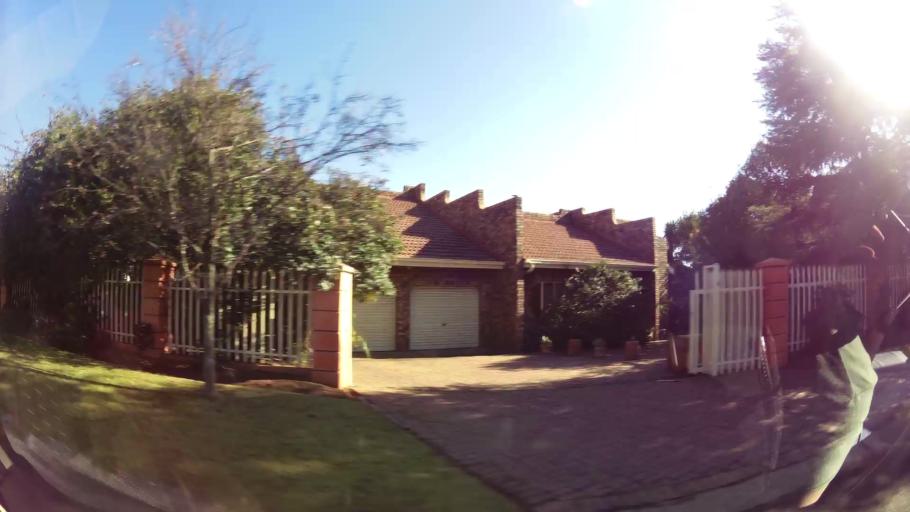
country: ZA
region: Mpumalanga
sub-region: Nkangala District Municipality
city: Witbank
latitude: -25.8866
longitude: 29.2541
